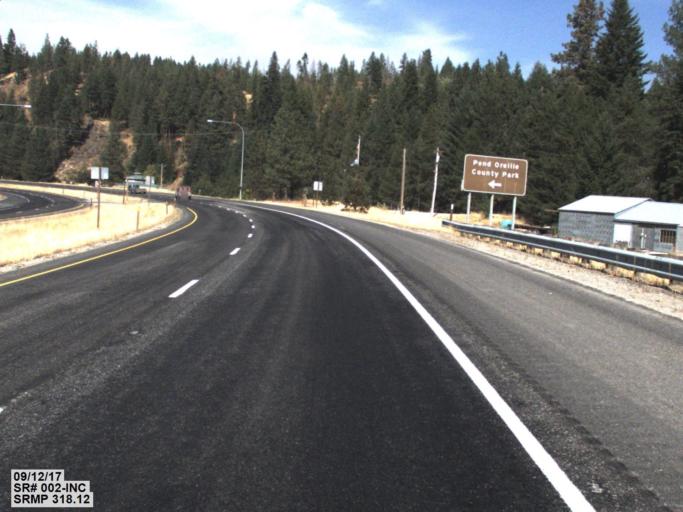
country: US
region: Washington
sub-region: Spokane County
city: Deer Park
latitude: 48.0798
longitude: -117.3244
